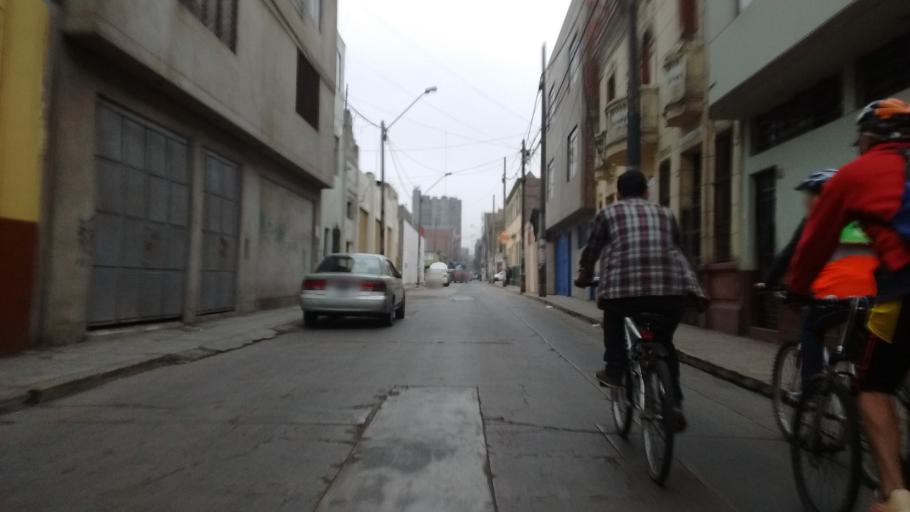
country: PE
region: Lima
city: Lima
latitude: -12.0641
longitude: -77.0284
